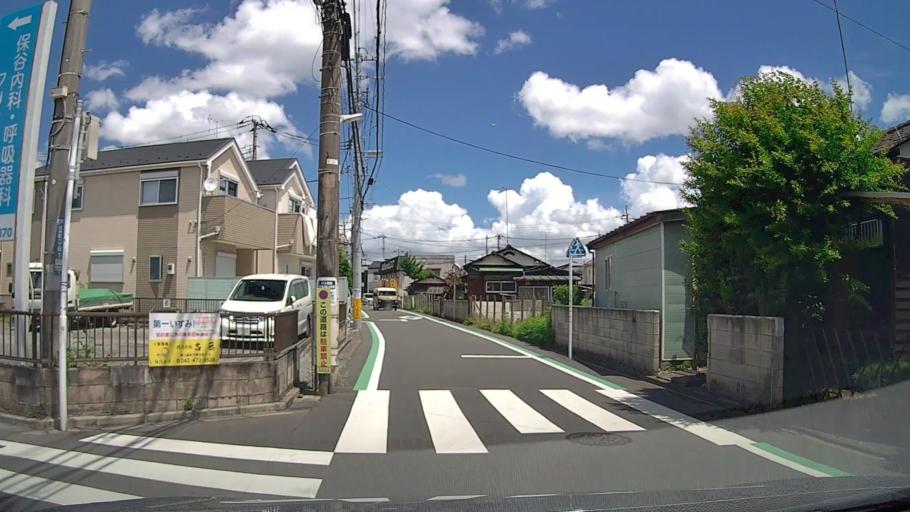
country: JP
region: Tokyo
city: Tanashicho
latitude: 35.7432
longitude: 139.5518
